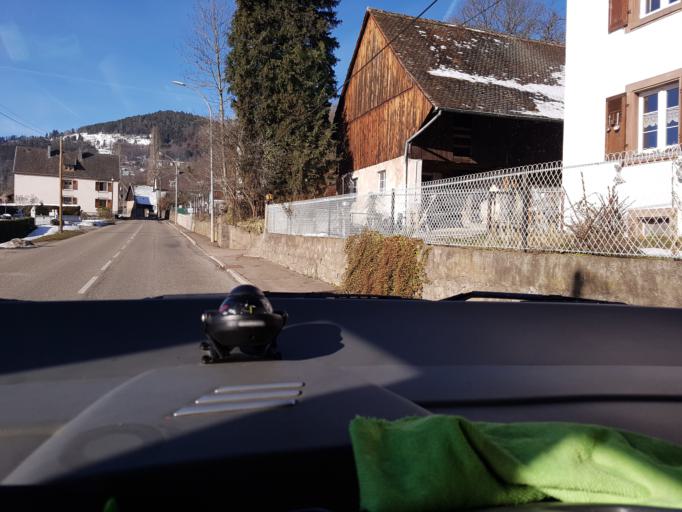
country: FR
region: Alsace
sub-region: Departement du Haut-Rhin
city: Metzeral
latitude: 48.0260
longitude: 7.0927
